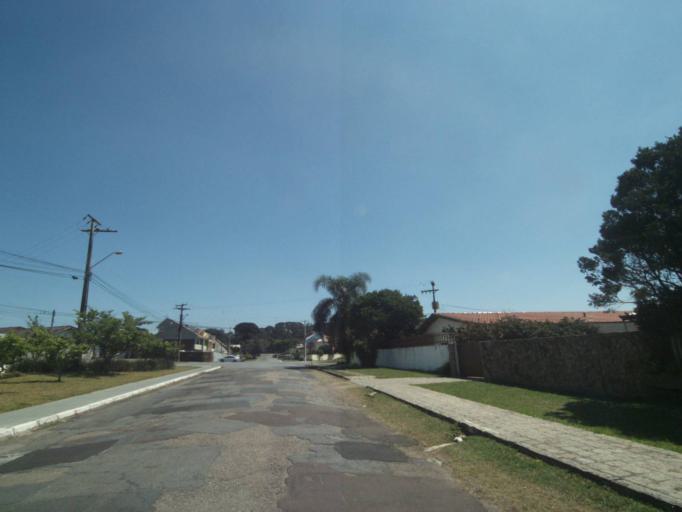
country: BR
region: Parana
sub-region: Sao Jose Dos Pinhais
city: Sao Jose dos Pinhais
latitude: -25.5112
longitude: -49.2393
